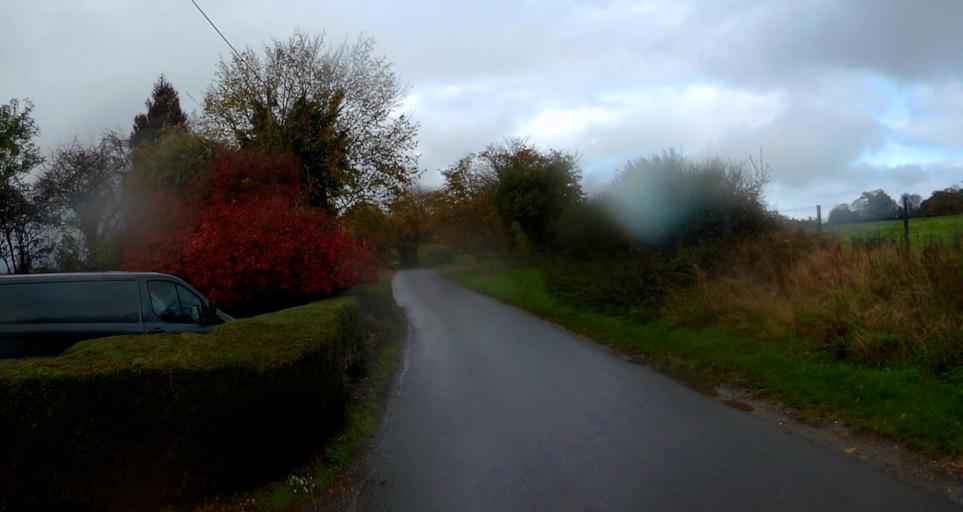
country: GB
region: England
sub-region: Hampshire
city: Four Marks
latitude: 51.1597
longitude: -1.0504
